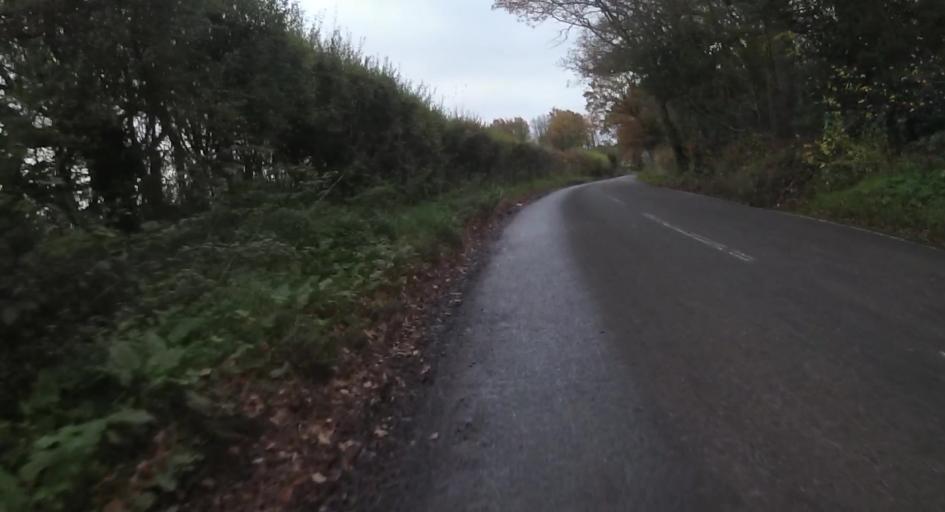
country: GB
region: England
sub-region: Wokingham
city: Shinfield
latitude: 51.3845
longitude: -0.9357
